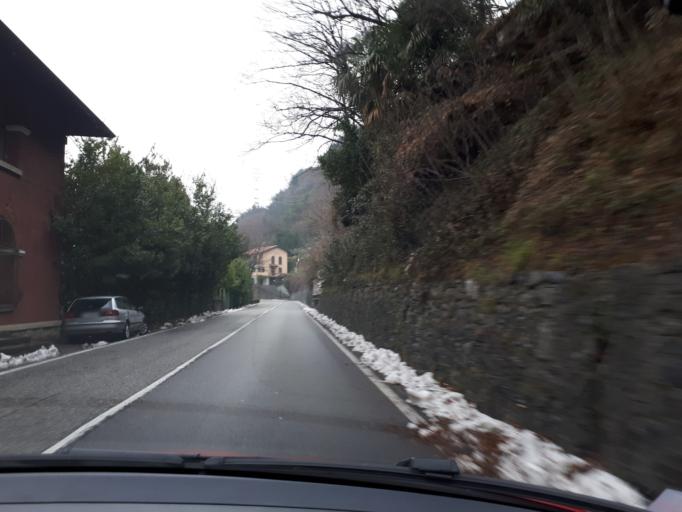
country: IT
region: Lombardy
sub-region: Provincia di Lecco
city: Lierna
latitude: 45.9735
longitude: 9.2987
